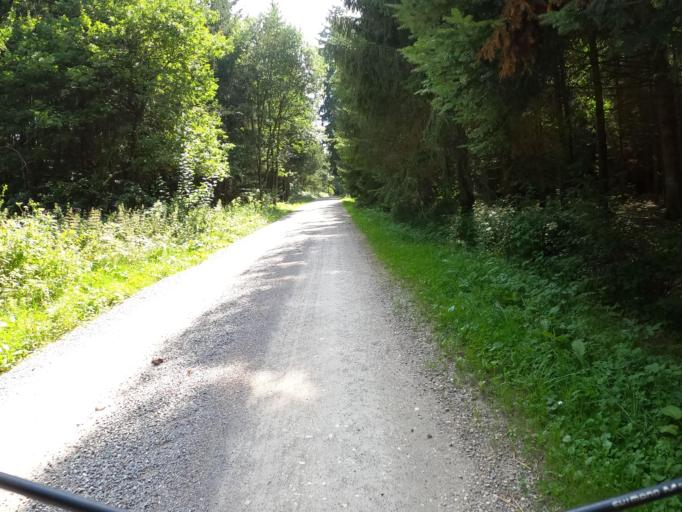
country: DE
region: Bavaria
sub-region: Swabia
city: Rieden an der Kotz
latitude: 48.3738
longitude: 10.2262
